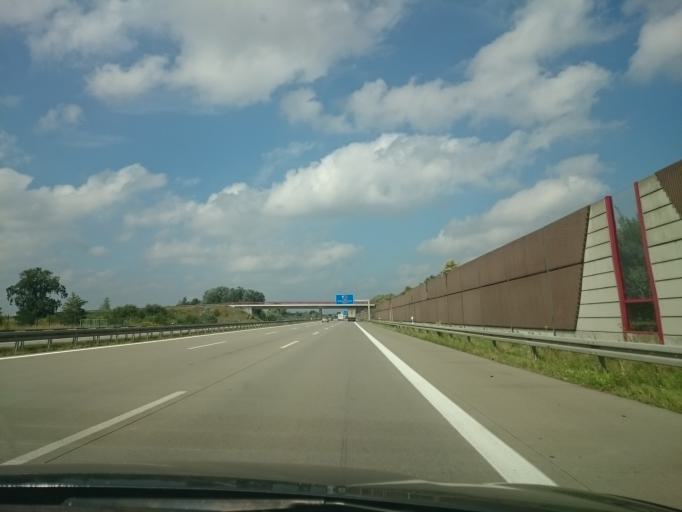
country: DE
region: Brandenburg
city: Ahrensfelde
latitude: 52.5922
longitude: 13.6195
